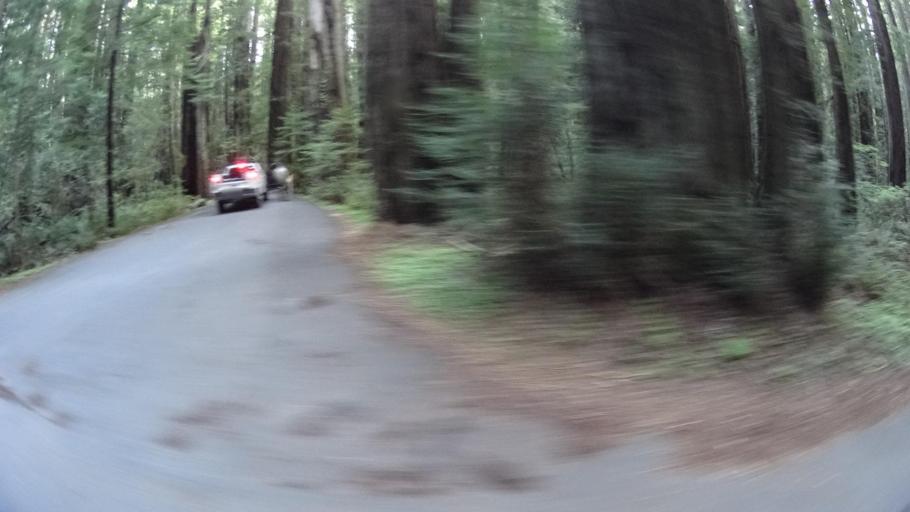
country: US
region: California
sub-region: Humboldt County
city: Rio Dell
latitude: 40.3514
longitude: -124.0022
